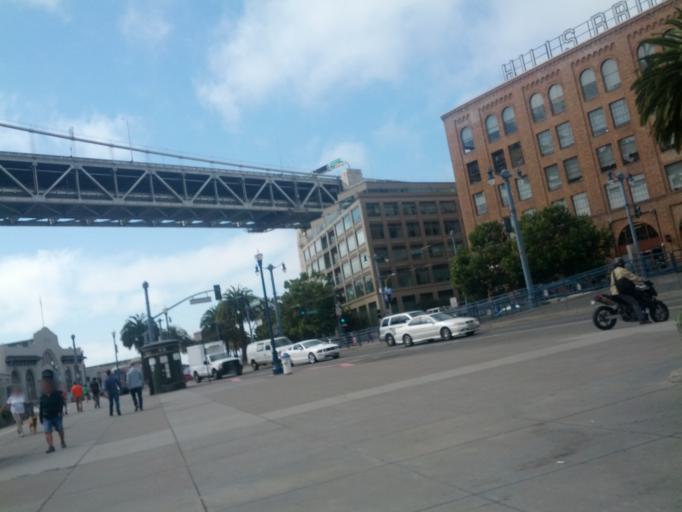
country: US
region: California
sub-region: San Francisco County
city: San Francisco
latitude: 37.7903
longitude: -122.3887
